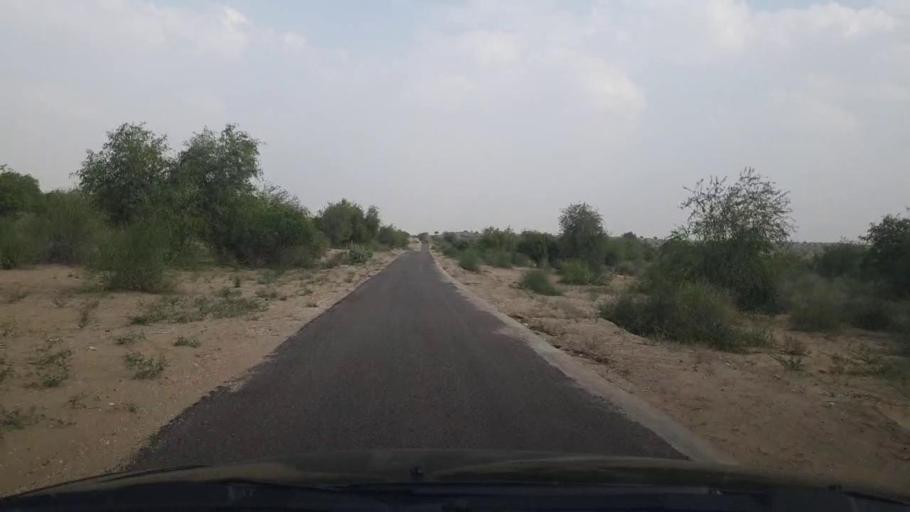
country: PK
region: Sindh
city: Islamkot
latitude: 25.0076
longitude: 70.6533
